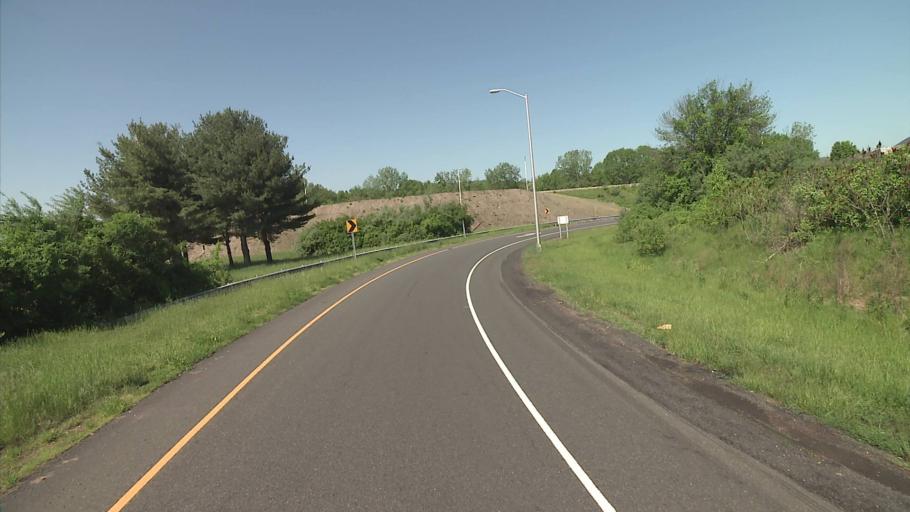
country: US
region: Connecticut
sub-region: New Haven County
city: Cheshire Village
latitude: 41.5623
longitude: -72.9155
